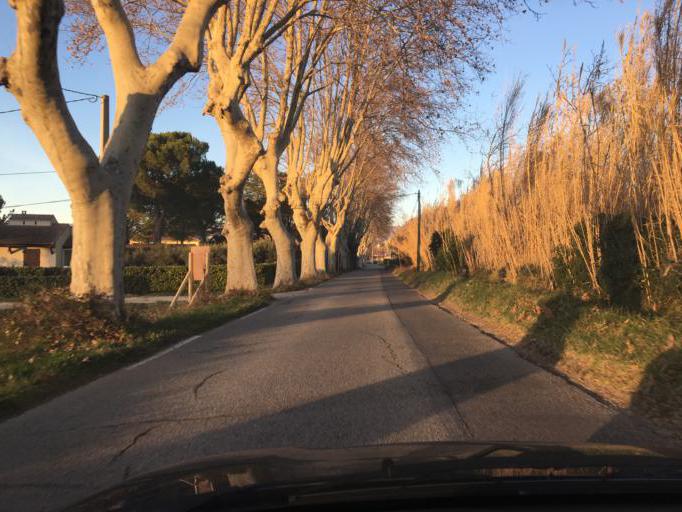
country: FR
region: Provence-Alpes-Cote d'Azur
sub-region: Departement des Bouches-du-Rhone
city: Mallemort
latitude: 43.7221
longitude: 5.1757
